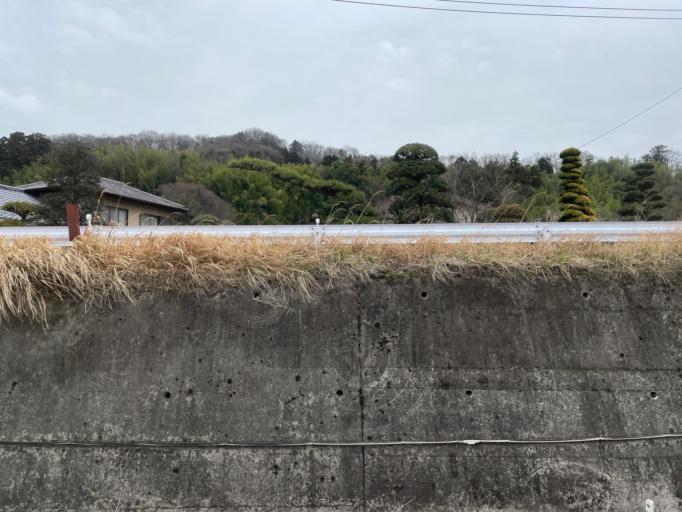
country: JP
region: Gunma
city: Numata
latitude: 36.5585
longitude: 139.0444
